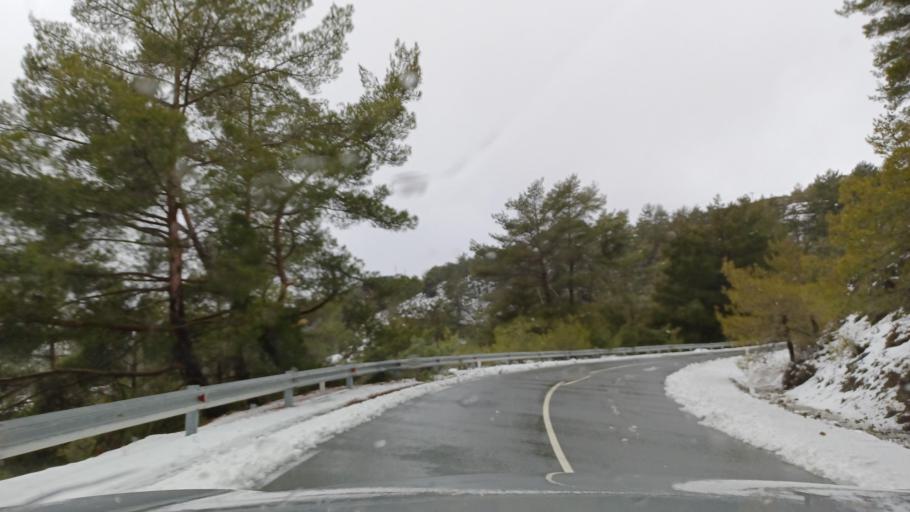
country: CY
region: Limassol
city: Pelendri
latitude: 34.8851
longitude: 32.9497
